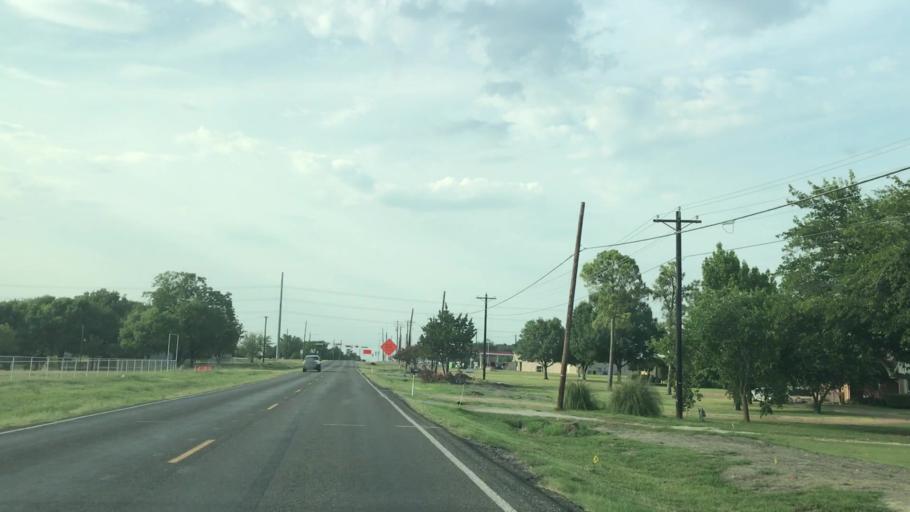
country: US
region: Texas
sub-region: Rockwall County
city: Fate
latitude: 32.9335
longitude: -96.4180
